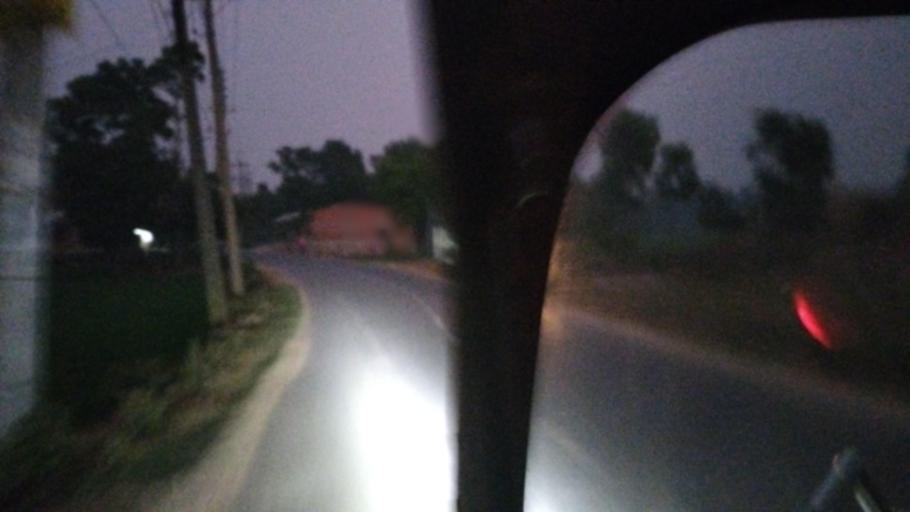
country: BD
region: Dhaka
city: Sakhipur
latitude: 24.3997
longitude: 90.3448
